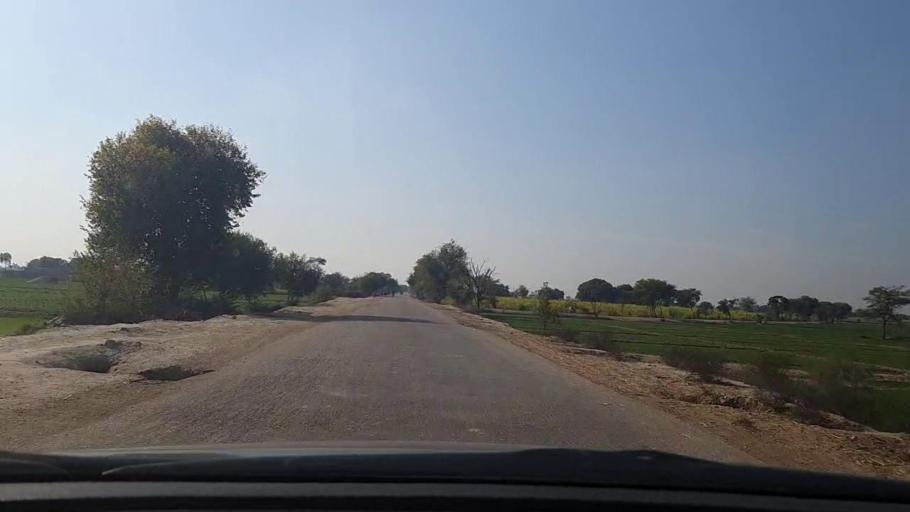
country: PK
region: Sindh
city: Daulatpur
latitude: 26.3193
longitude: 68.0502
